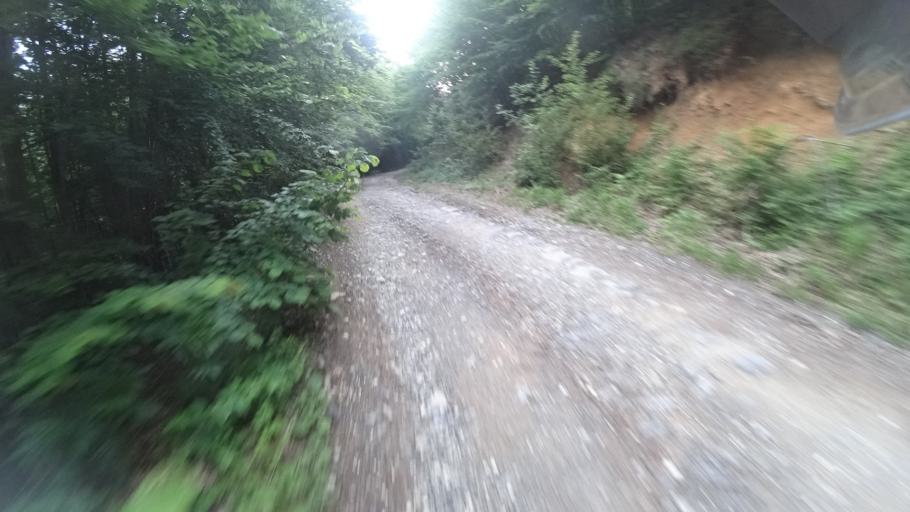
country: HR
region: Licko-Senjska
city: Gospic
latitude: 44.4781
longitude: 15.3126
